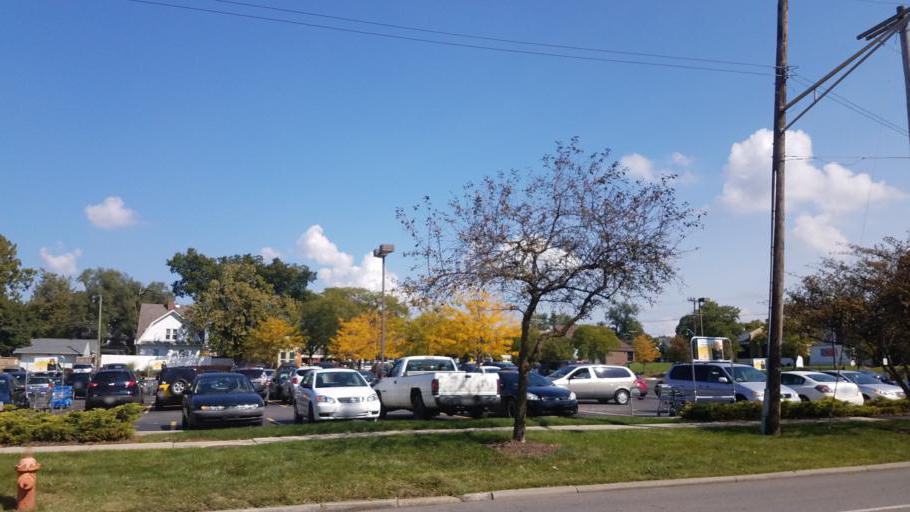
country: US
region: Ohio
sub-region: Franklin County
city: Grandview Heights
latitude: 40.0316
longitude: -83.0170
